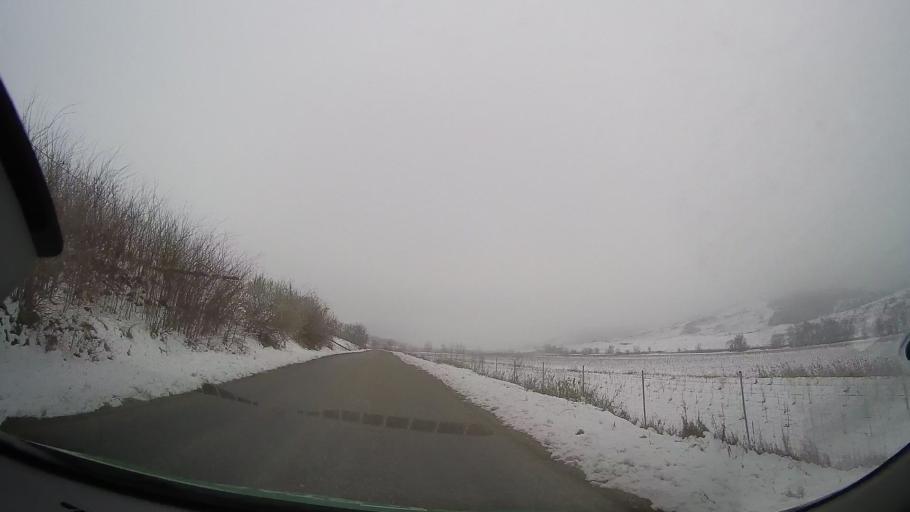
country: RO
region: Bacau
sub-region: Comuna Vultureni
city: Vultureni
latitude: 46.3641
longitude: 27.2860
